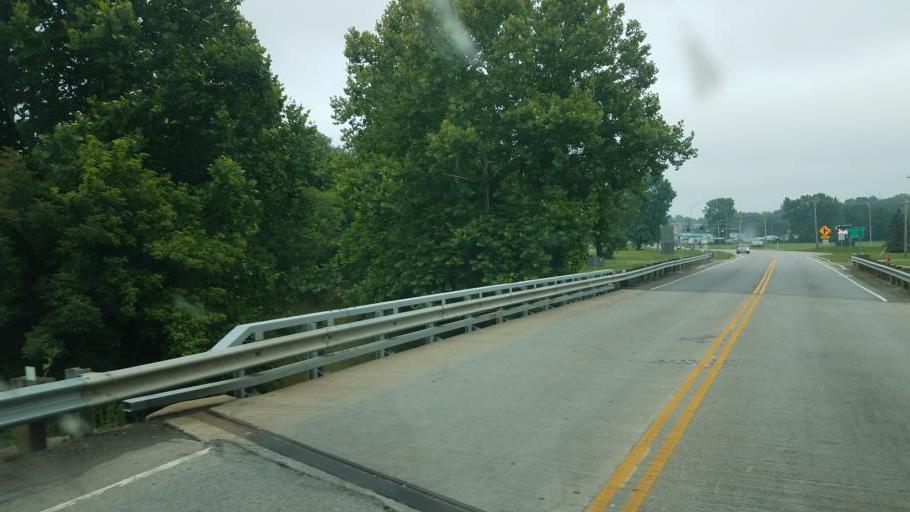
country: US
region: Ohio
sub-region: Highland County
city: Hillsboro
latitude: 39.2367
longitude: -83.6089
